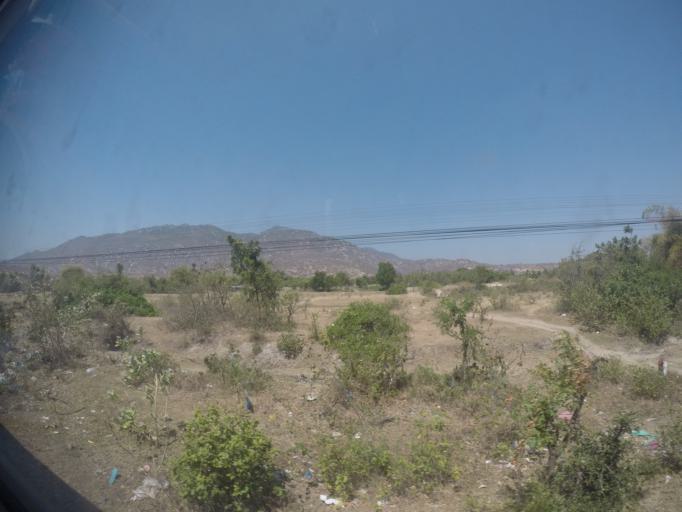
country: VN
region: Ninh Thuan
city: Phuoc Dan
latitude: 11.3859
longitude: 108.8834
